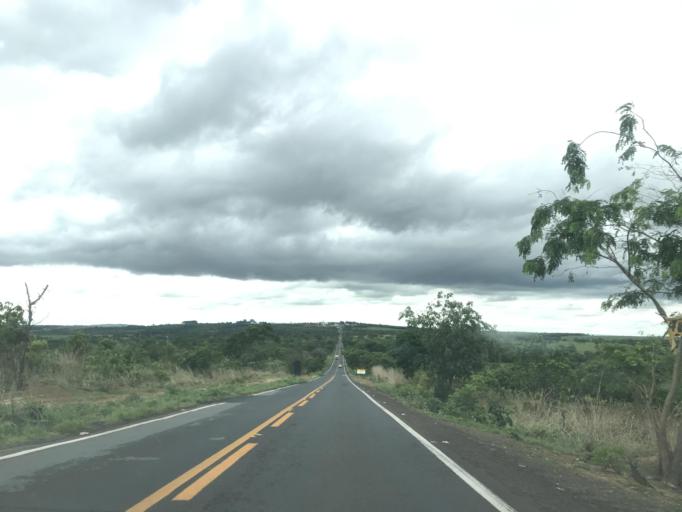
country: BR
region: Goias
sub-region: Caldas Novas
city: Caldas Novas
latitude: -17.6964
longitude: -48.7072
